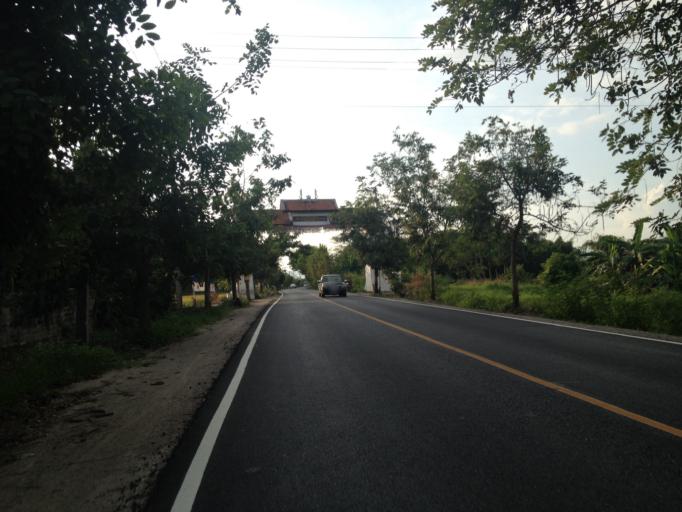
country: TH
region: Chiang Mai
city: Hang Dong
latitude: 18.6834
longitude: 98.9749
